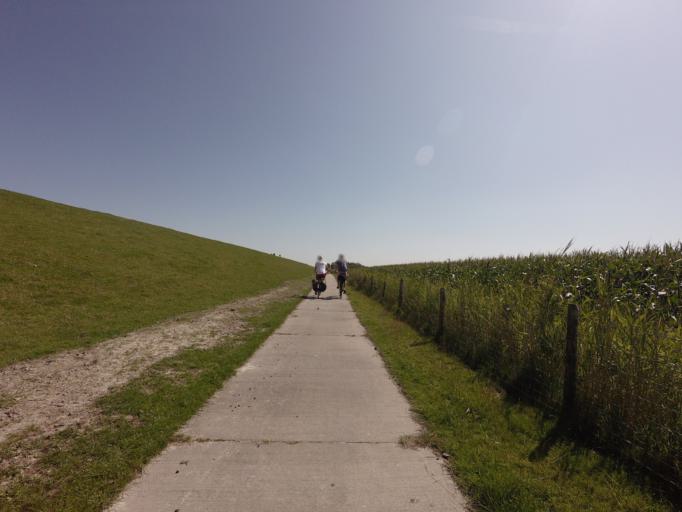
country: NL
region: Friesland
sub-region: Gemeente Dongeradeel
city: Anjum
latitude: 53.3997
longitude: 6.0991
